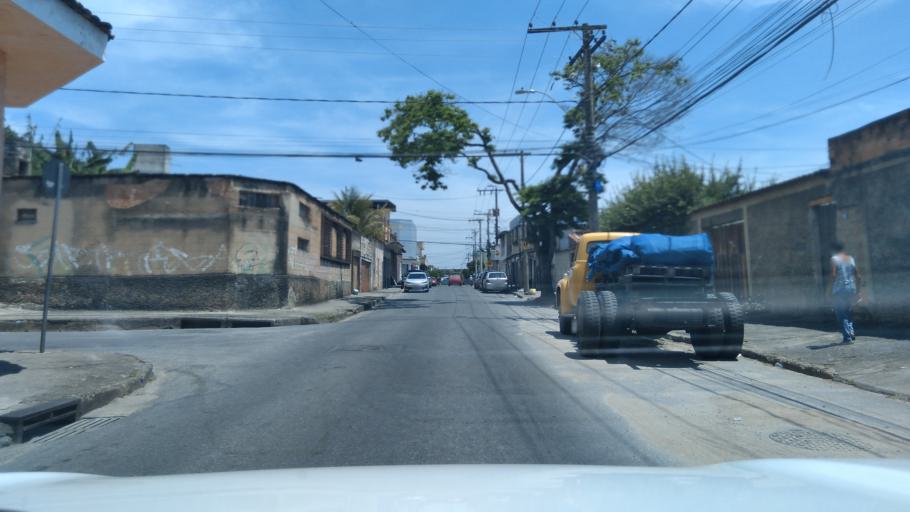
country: BR
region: Minas Gerais
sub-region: Contagem
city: Contagem
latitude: -19.8989
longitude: -44.0106
